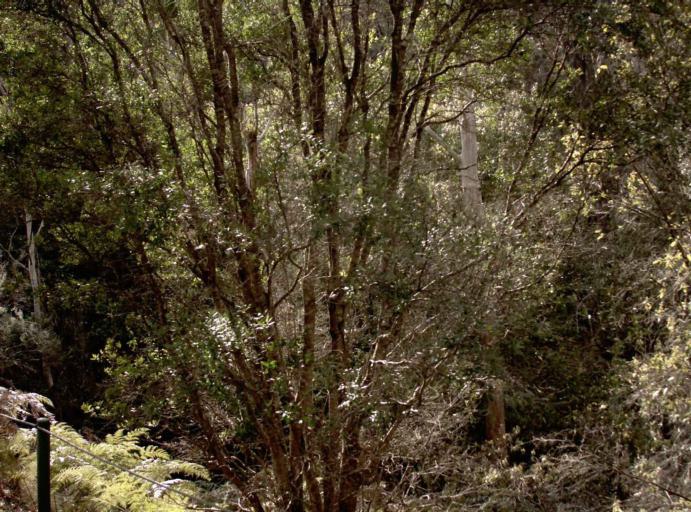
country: AU
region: Tasmania
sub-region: Launceston
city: West Launceston
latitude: -41.4433
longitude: 147.1166
